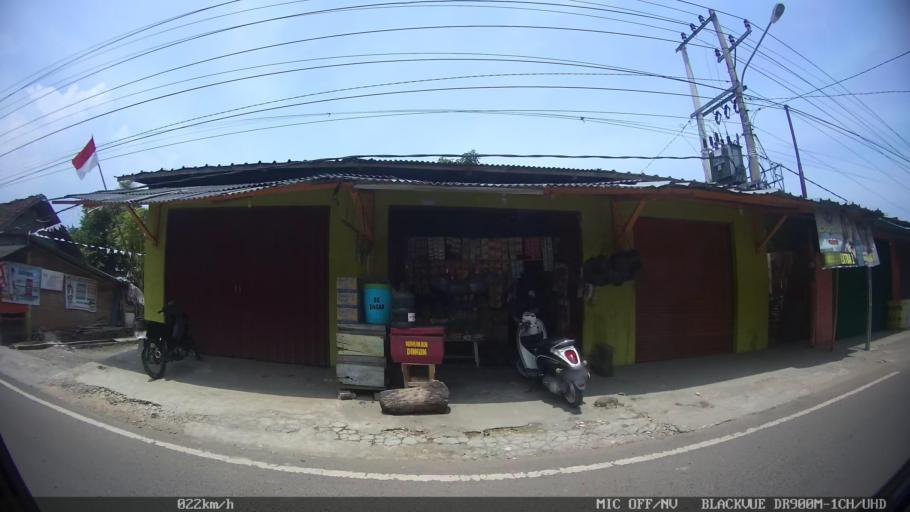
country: ID
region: Lampung
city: Bandarlampung
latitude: -5.4567
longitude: 105.2457
